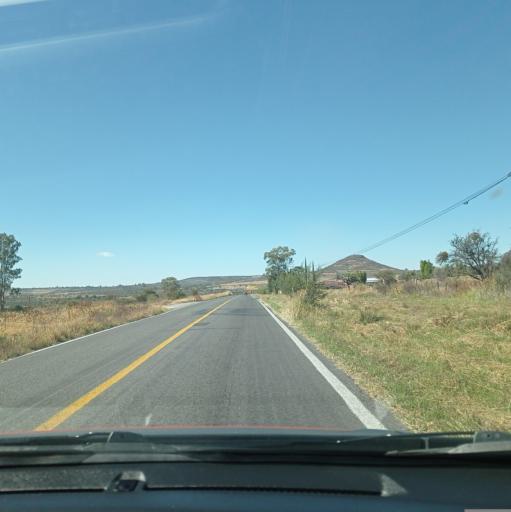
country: MX
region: Jalisco
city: San Diego de Alejandria
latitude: 21.0045
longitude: -102.0793
